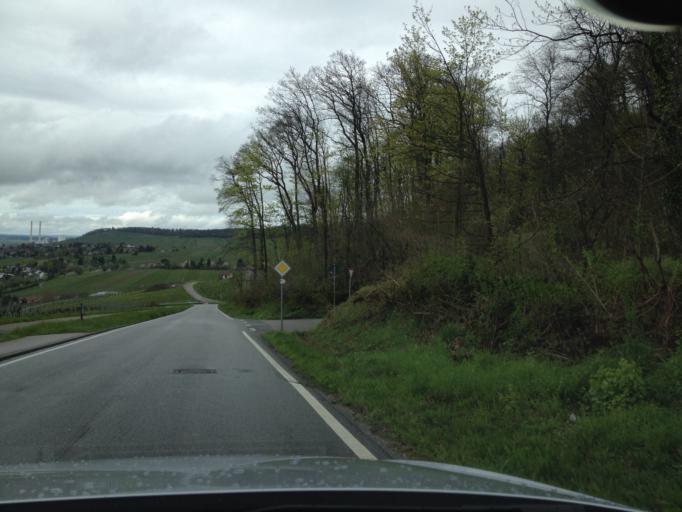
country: DE
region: Baden-Wuerttemberg
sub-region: Regierungsbezirk Stuttgart
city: Weinsberg
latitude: 49.1336
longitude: 9.2642
